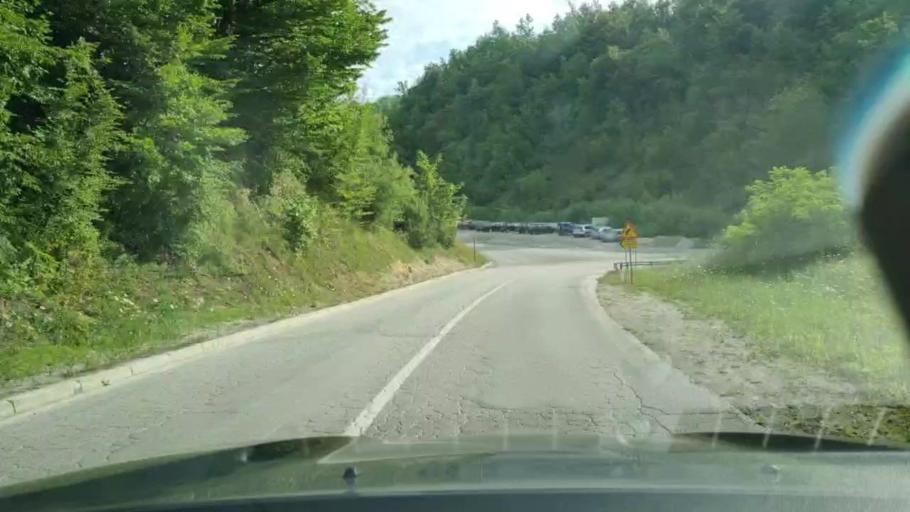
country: BA
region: Federation of Bosnia and Herzegovina
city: Buzim
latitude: 45.0330
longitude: 16.0593
